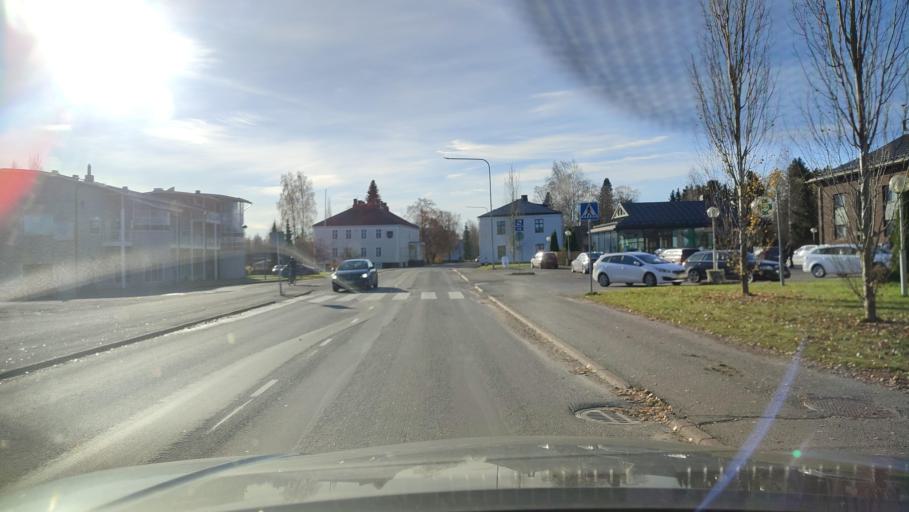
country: FI
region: Southern Ostrobothnia
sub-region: Suupohja
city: Teuva
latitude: 62.4860
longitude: 21.7464
